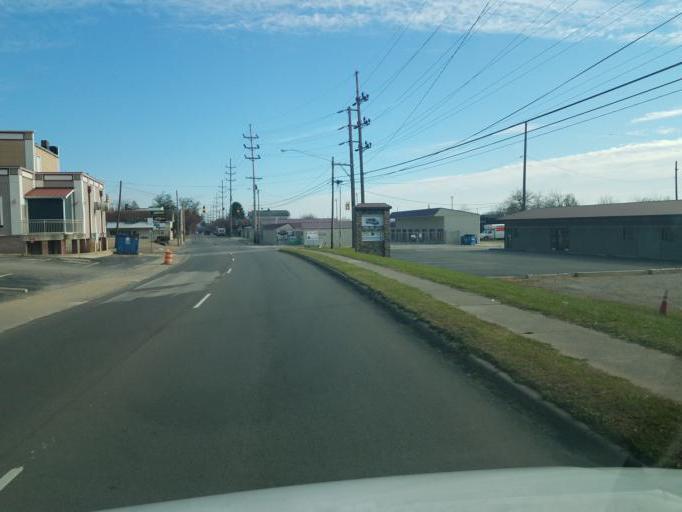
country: US
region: Kentucky
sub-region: Greenup County
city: South Shore
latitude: 38.7418
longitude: -82.9580
